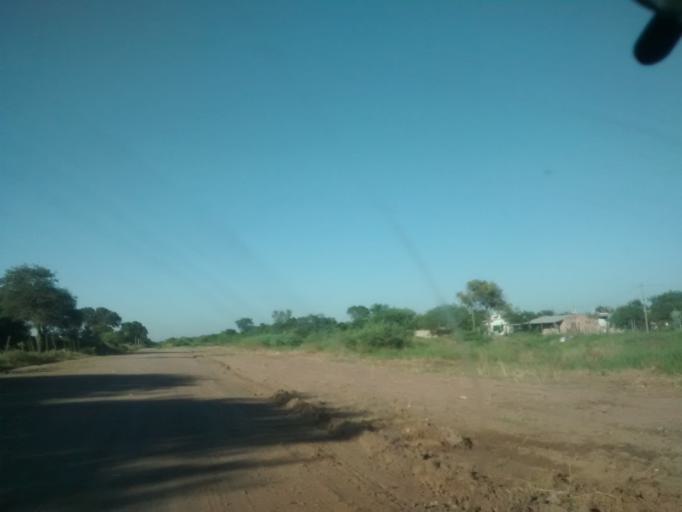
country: AR
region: Chaco
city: Resistencia
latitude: -27.4661
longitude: -59.0318
